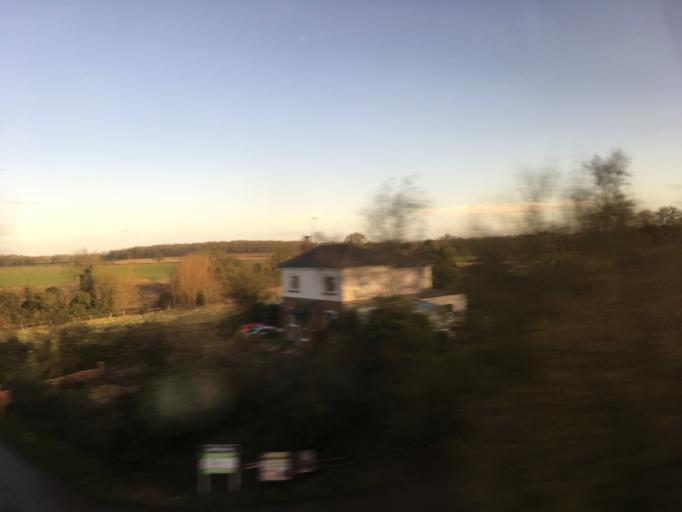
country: GB
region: England
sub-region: Wiltshire
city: Norton
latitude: 51.5447
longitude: -2.1496
